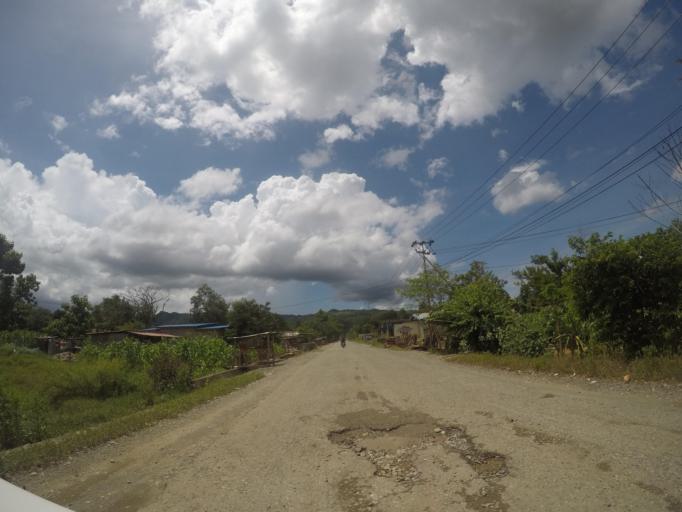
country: TL
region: Bobonaro
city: Maliana
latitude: -8.9620
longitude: 125.1193
